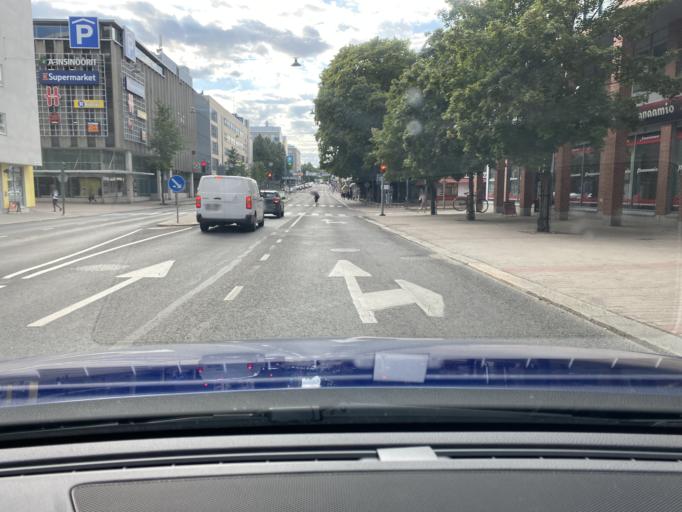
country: FI
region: Pirkanmaa
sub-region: Tampere
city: Tampere
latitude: 61.5006
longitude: 23.7571
